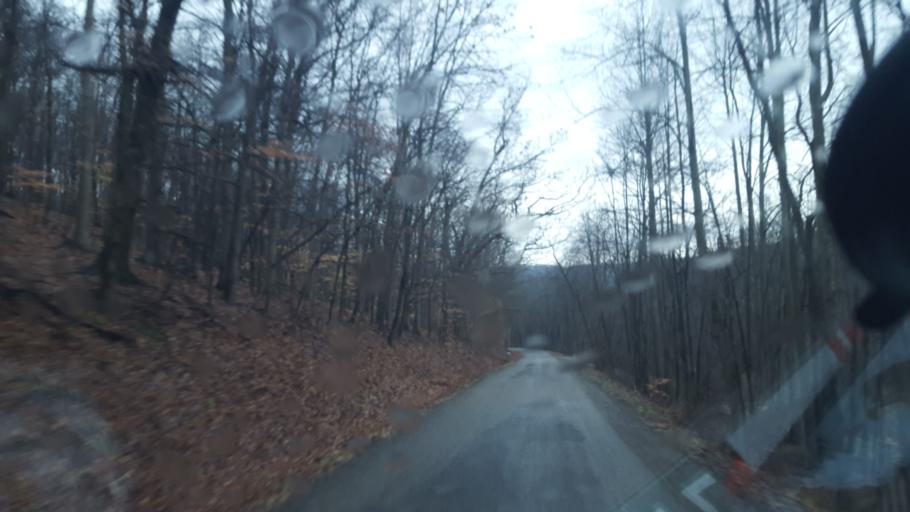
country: US
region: Ohio
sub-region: Tuscarawas County
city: Newcomerstown
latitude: 40.2706
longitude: -81.5091
